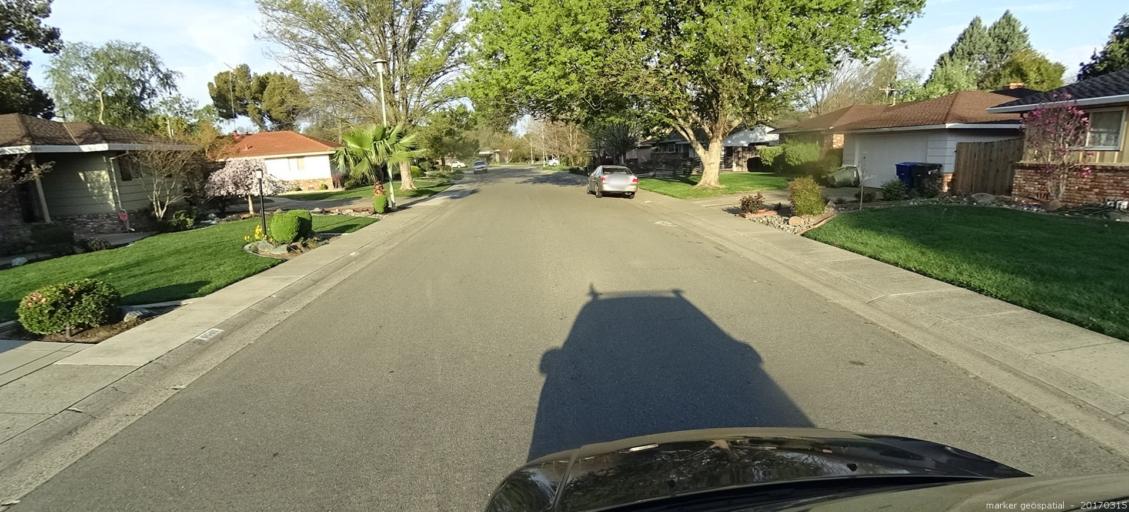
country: US
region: California
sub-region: Sacramento County
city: Parkway
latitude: 38.5081
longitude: -121.5123
